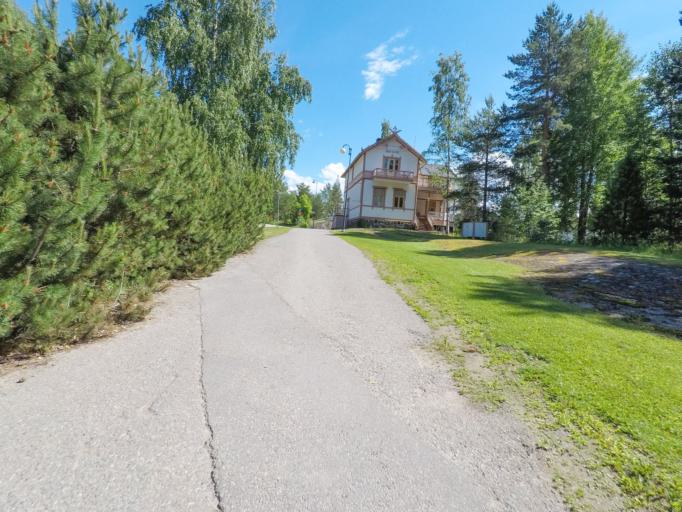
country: FI
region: Southern Savonia
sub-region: Savonlinna
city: Savonlinna
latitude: 61.8699
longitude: 28.8906
